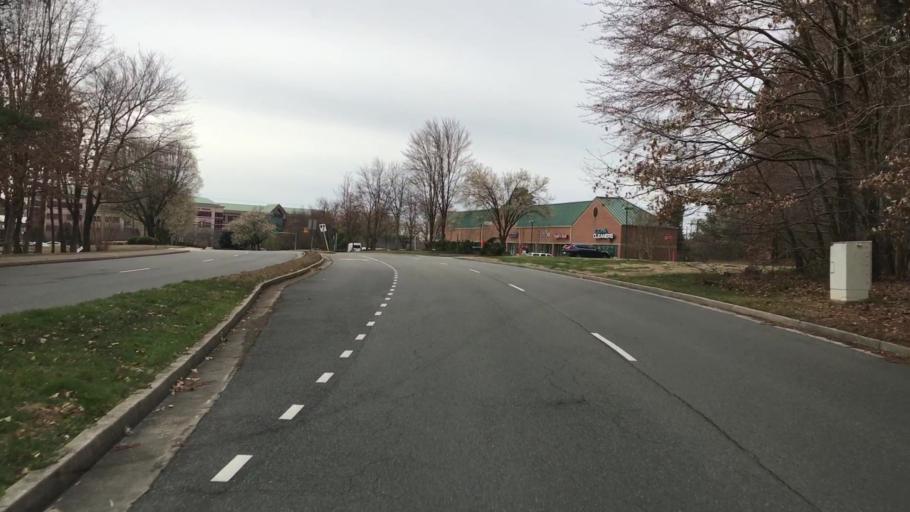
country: US
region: Virginia
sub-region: Henrico County
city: Short Pump
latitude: 37.6477
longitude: -77.5749
